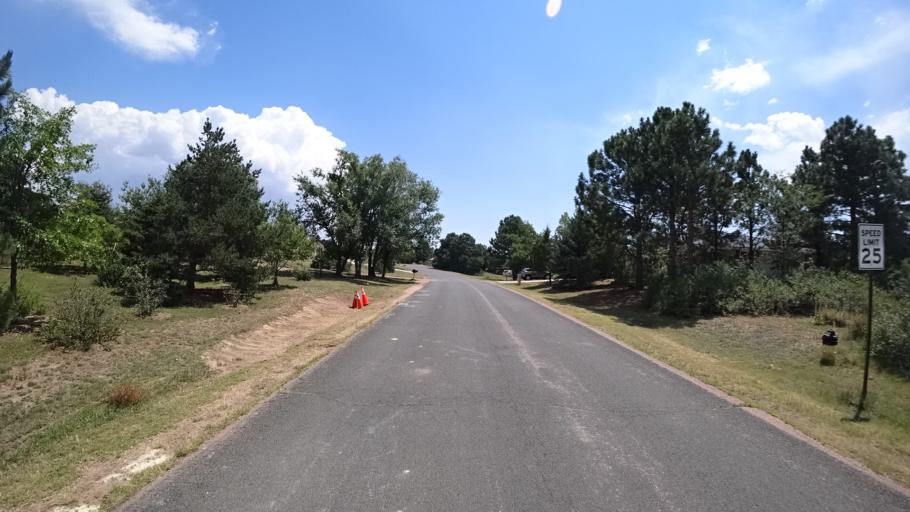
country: US
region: Colorado
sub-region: El Paso County
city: Air Force Academy
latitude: 38.9385
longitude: -104.8023
